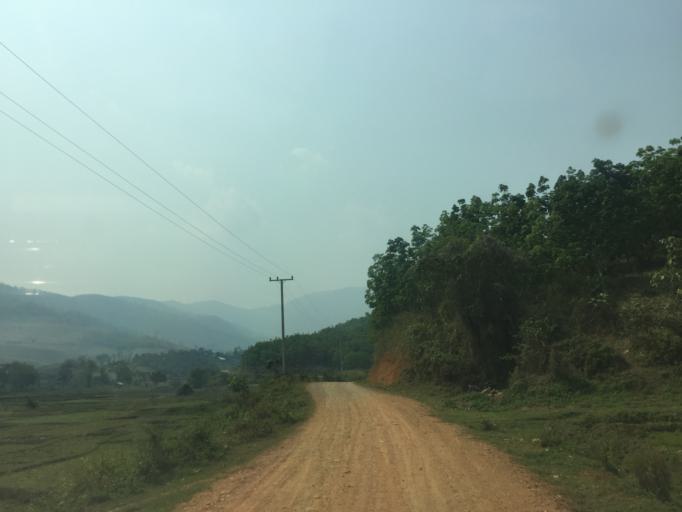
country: TH
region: Phayao
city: Phu Sang
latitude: 19.5744
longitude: 100.5256
